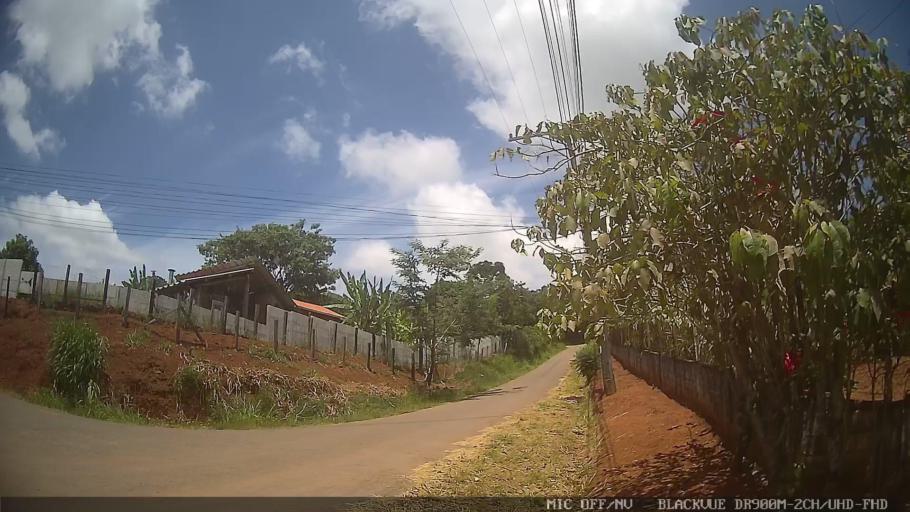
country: BR
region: Sao Paulo
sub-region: Braganca Paulista
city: Braganca Paulista
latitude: -23.0226
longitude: -46.5418
